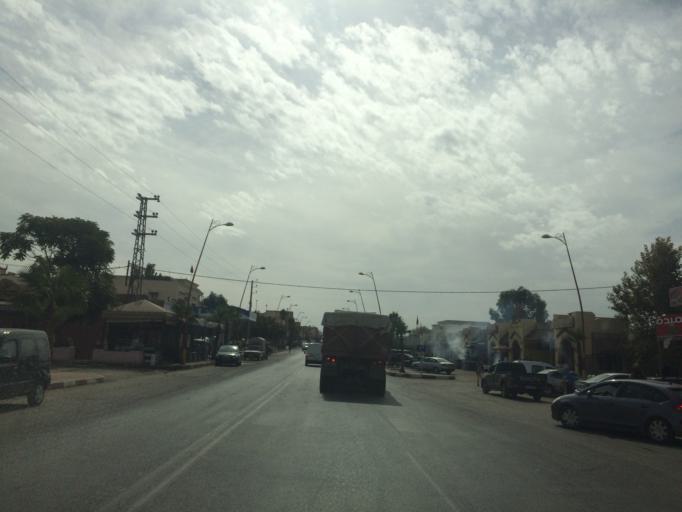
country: MA
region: Meknes-Tafilalet
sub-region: El-Hajeb
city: El Hajeb
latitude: 33.7624
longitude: -5.4861
